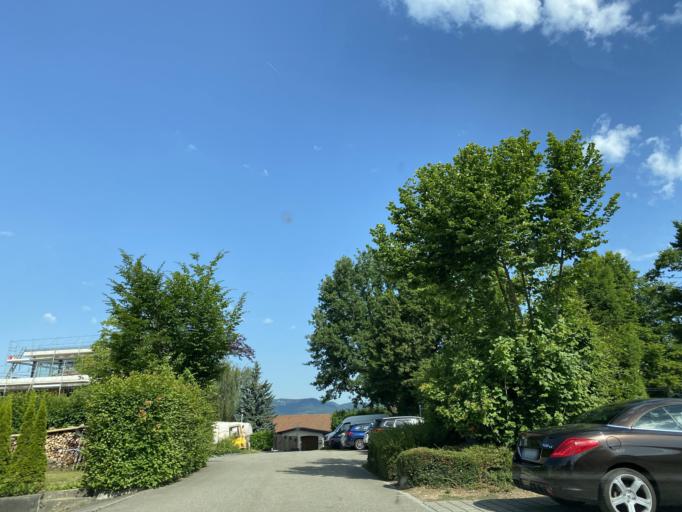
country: CH
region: Aargau
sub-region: Bezirk Zofingen
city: Rothrist
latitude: 47.3005
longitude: 7.8805
